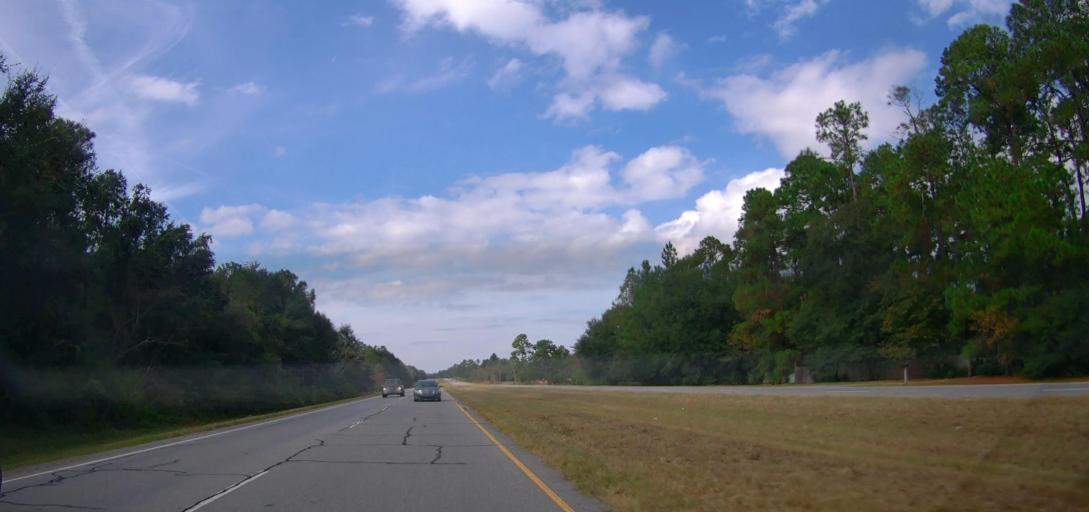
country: US
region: Georgia
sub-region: Mitchell County
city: Camilla
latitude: 31.2055
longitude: -84.1736
